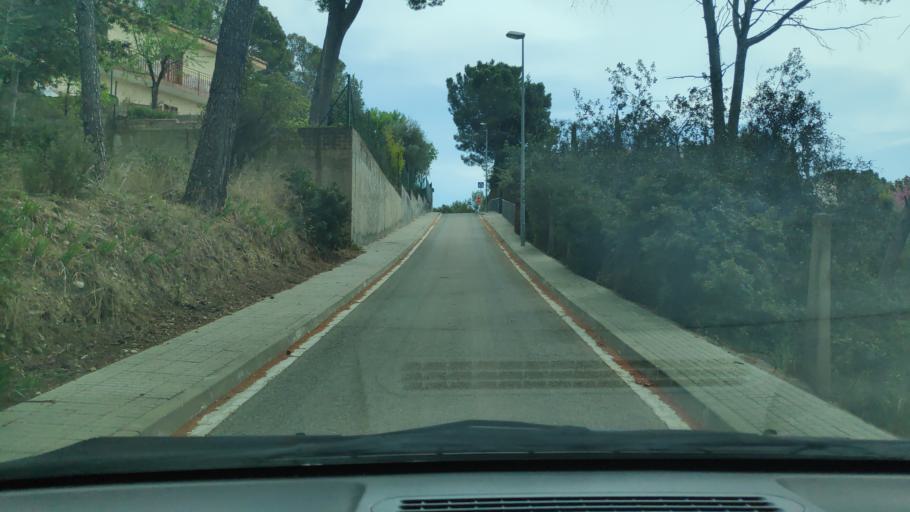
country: ES
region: Catalonia
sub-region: Provincia de Barcelona
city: Sant Quirze del Valles
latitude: 41.5114
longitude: 2.0605
